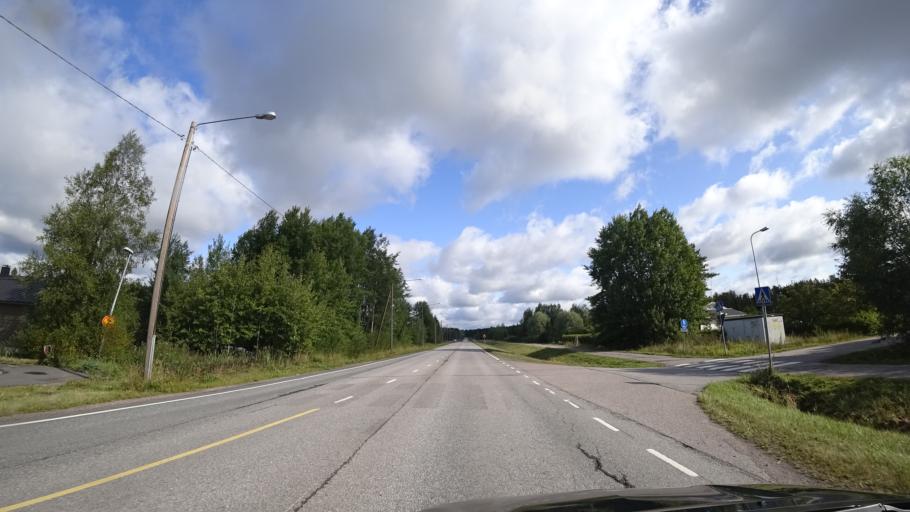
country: FI
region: Uusimaa
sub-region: Helsinki
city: Hyvinge
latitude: 60.5617
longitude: 24.9723
